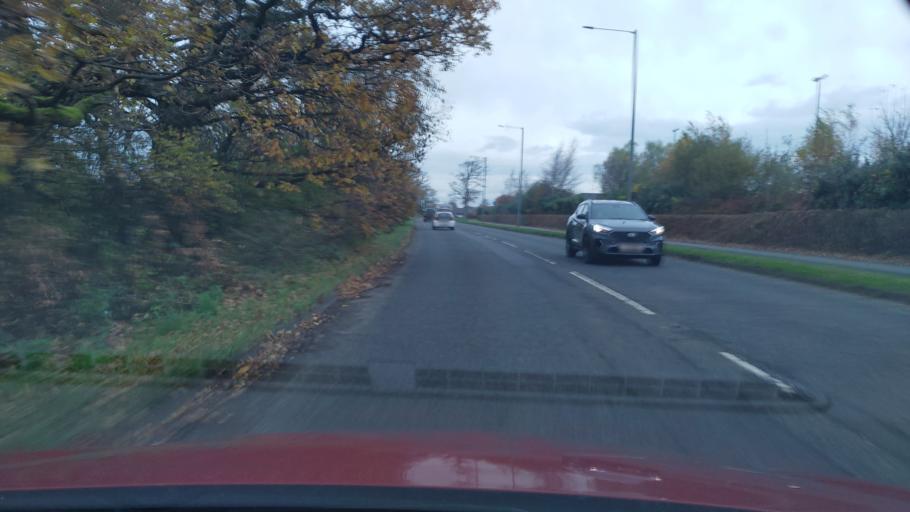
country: GB
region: England
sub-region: Lancashire
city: Euxton
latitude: 53.6838
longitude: -2.6764
